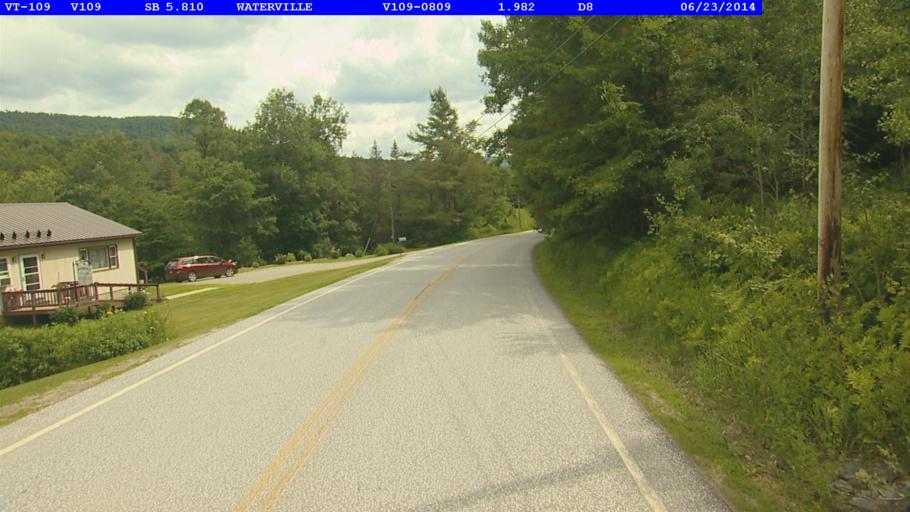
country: US
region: Vermont
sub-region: Lamoille County
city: Johnson
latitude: 44.7084
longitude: -72.7595
